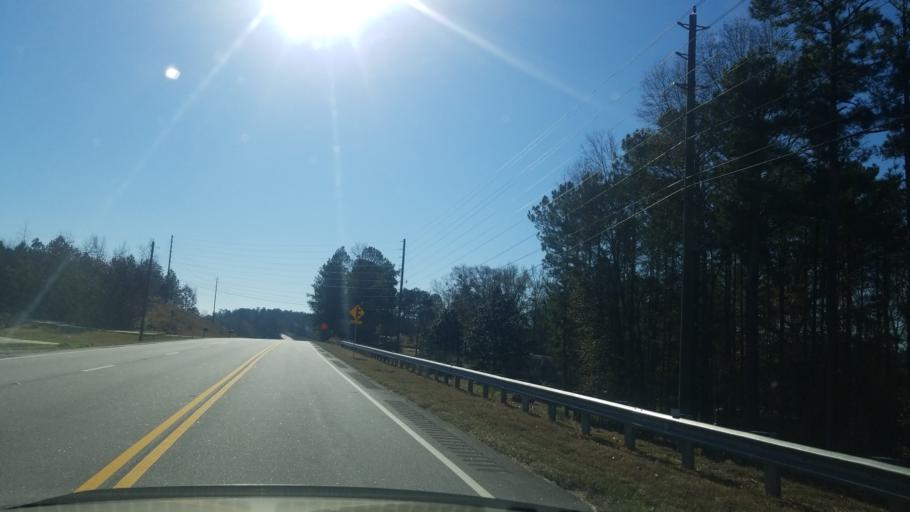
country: US
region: Alabama
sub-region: Chambers County
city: Valley
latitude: 32.8503
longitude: -85.1278
